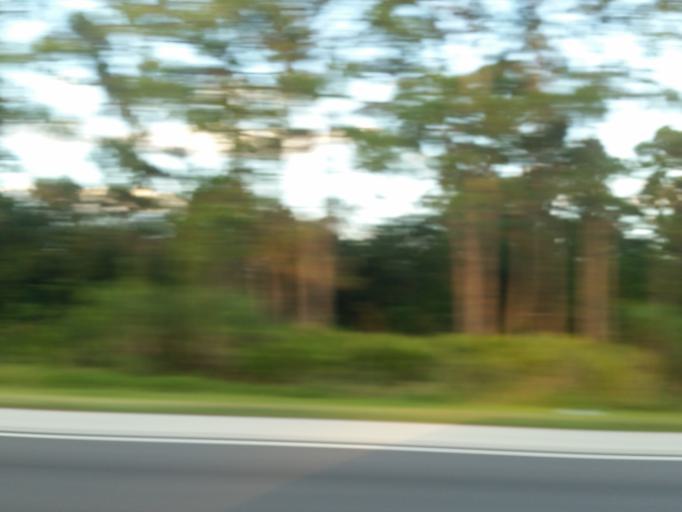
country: US
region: Florida
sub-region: Sarasota County
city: Vamo
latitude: 27.2321
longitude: -82.4520
